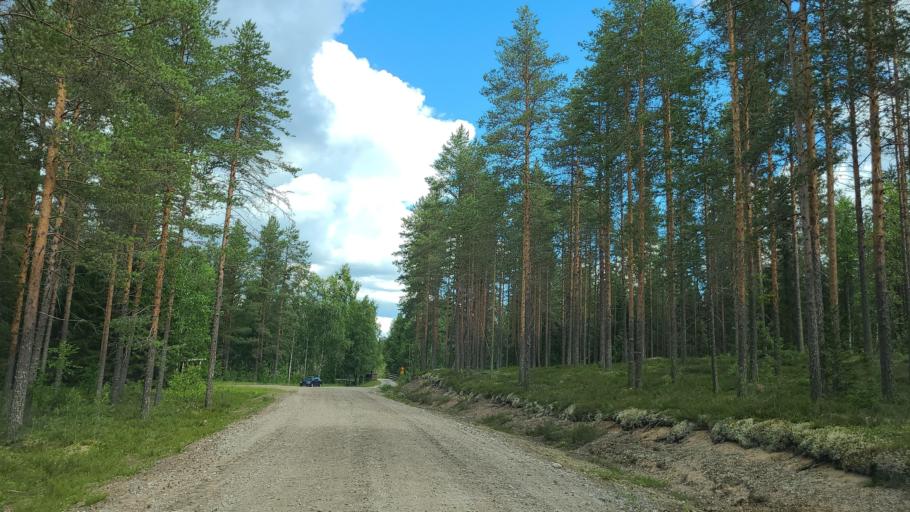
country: FI
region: Northern Savo
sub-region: Koillis-Savo
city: Kaavi
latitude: 63.0599
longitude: 28.8269
